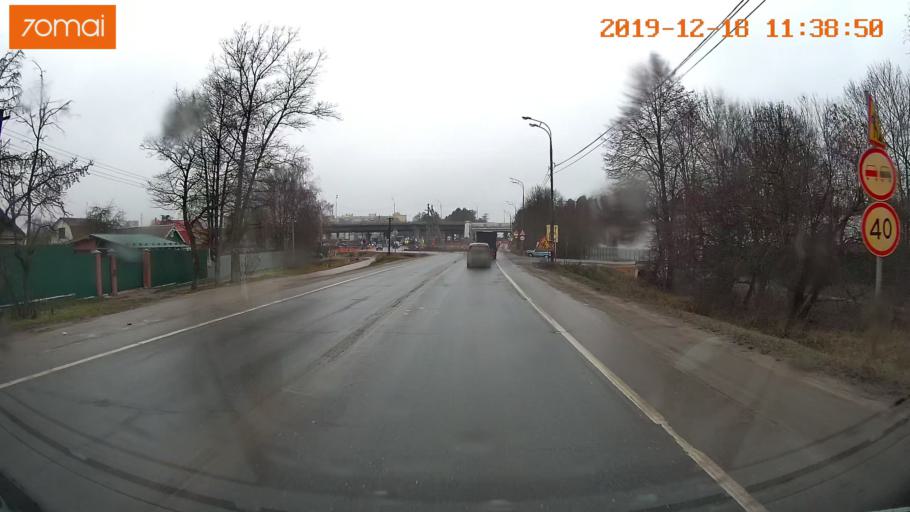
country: RU
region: Moskovskaya
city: Zvenigorod
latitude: 55.6987
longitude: 36.8846
